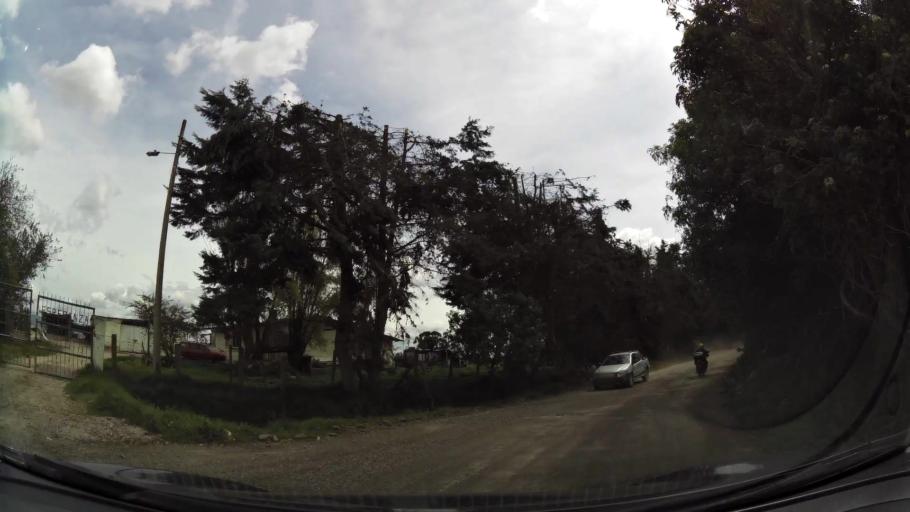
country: CO
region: Cundinamarca
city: Funza
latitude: 4.7130
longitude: -74.1746
